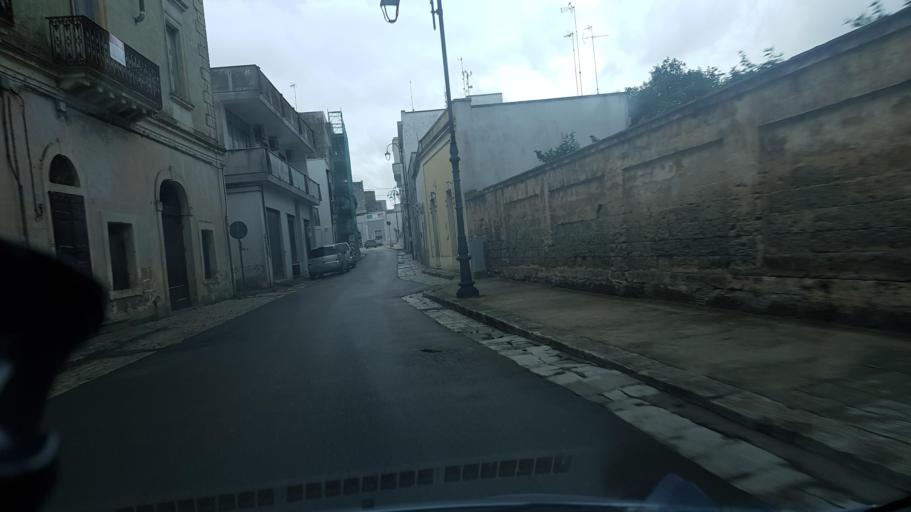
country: IT
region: Apulia
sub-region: Provincia di Lecce
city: Carmiano
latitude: 40.3472
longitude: 18.0471
